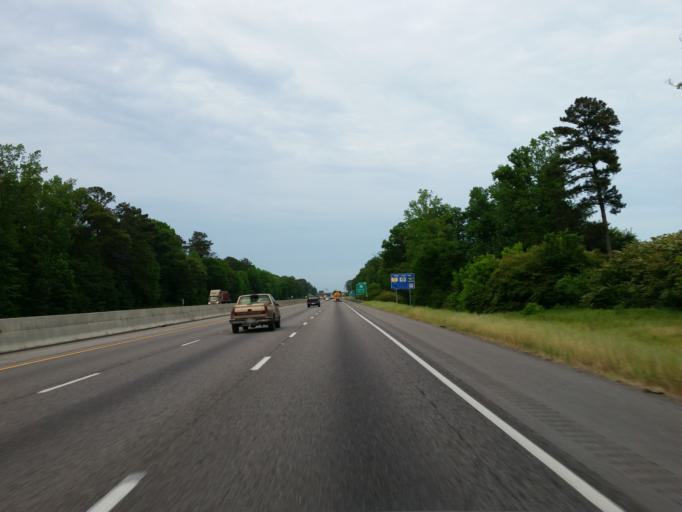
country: US
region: Alabama
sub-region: Saint Clair County
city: Pell City
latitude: 33.6037
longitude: -86.2978
